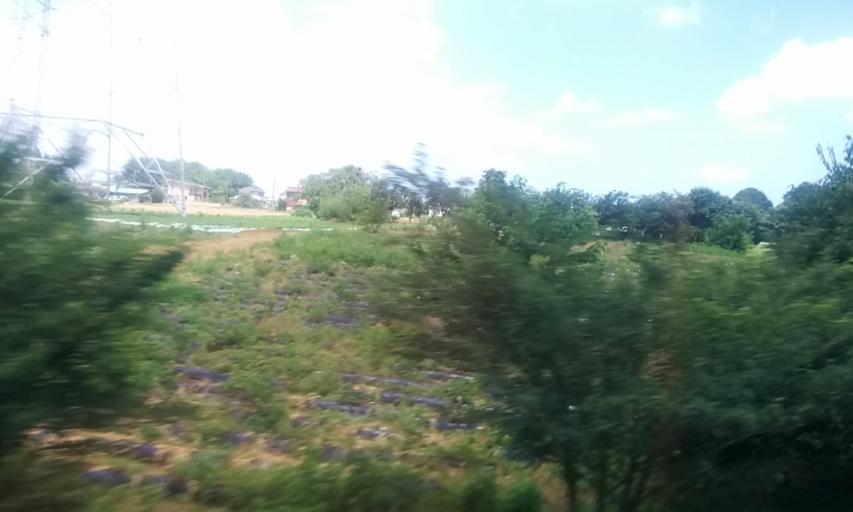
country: JP
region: Chiba
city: Oami
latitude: 35.5365
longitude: 140.2486
